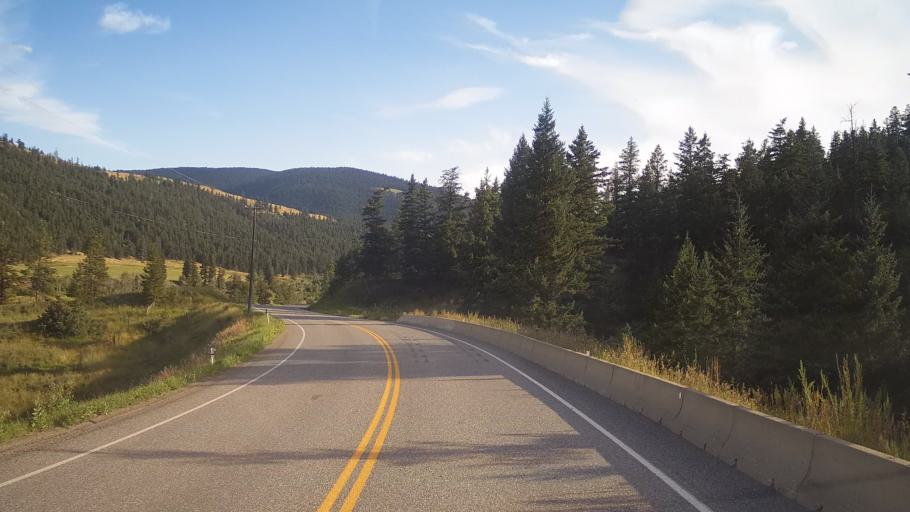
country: CA
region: British Columbia
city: Cache Creek
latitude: 50.8448
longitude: -121.5406
